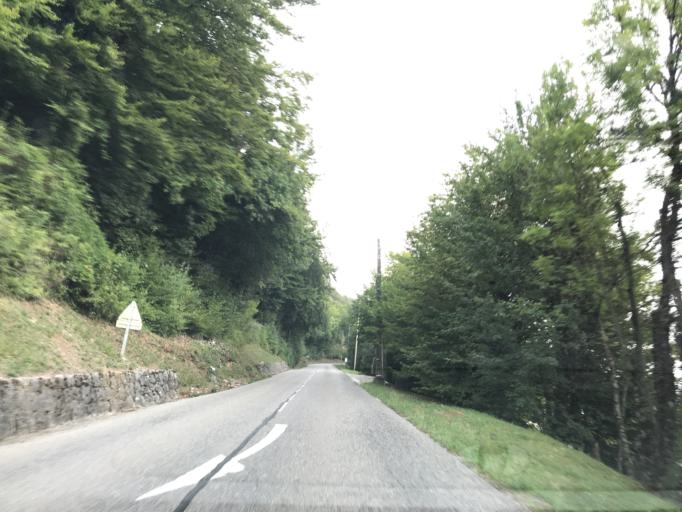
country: FR
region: Rhone-Alpes
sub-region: Departement de la Haute-Savoie
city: Talloires
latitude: 45.8497
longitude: 6.2185
